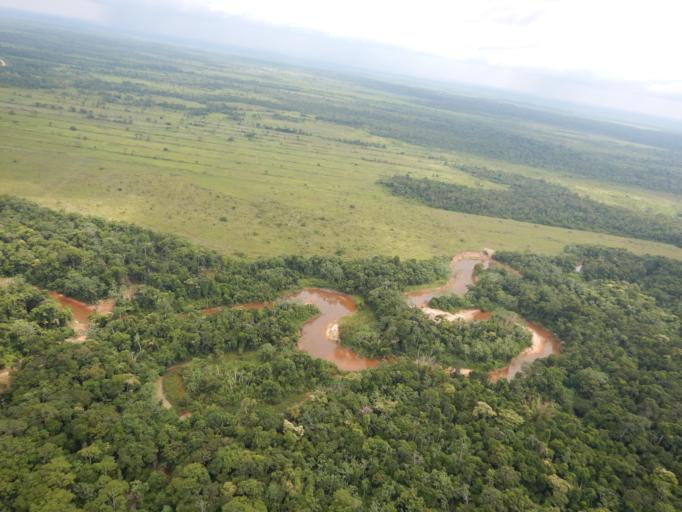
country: BO
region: Santa Cruz
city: Villa Yapacani
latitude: -17.1806
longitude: -64.2710
